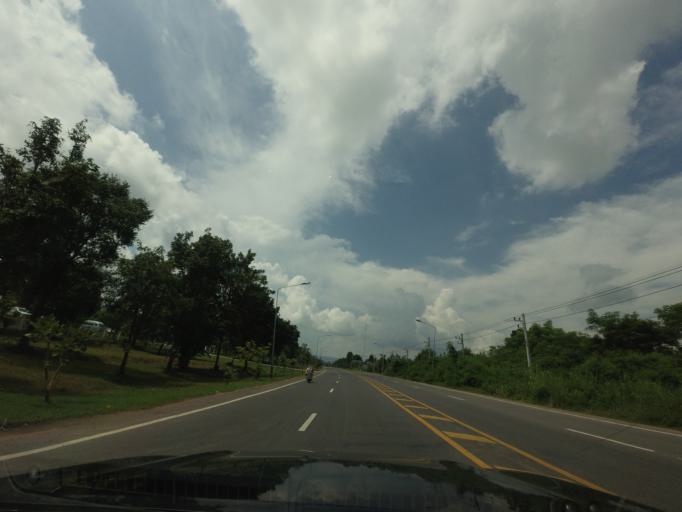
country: TH
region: Khon Kaen
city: Wiang Kao
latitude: 16.6761
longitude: 102.3280
